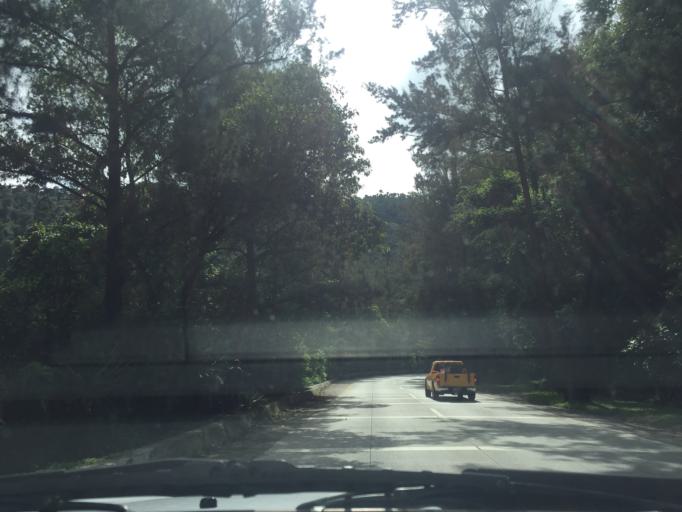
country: GT
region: Sacatepequez
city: Santa Lucia Milpas Altas
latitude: 14.5610
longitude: -90.7006
